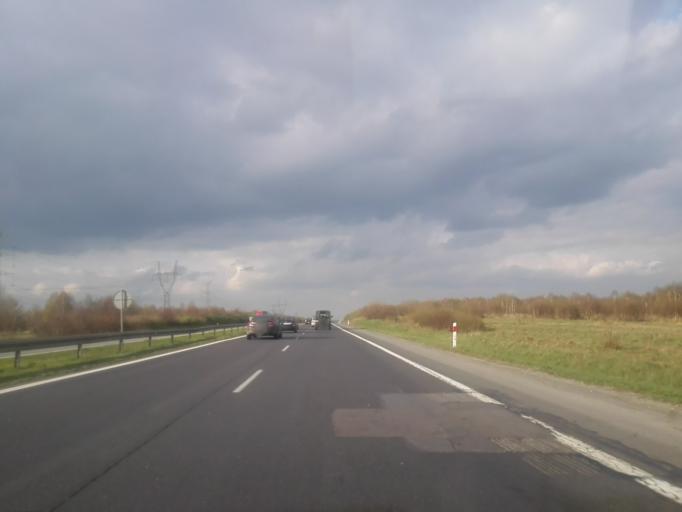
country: PL
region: Lodz Voivodeship
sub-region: Powiat radomszczanski
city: Radomsko
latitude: 51.0867
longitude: 19.3748
